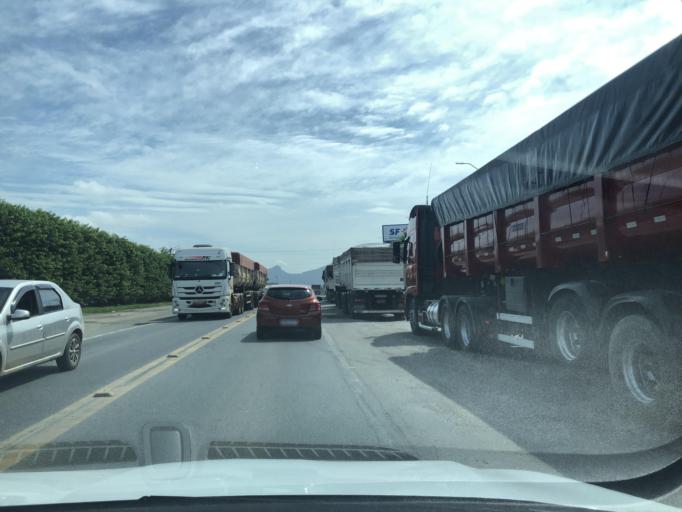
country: BR
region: Santa Catarina
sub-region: Sao Francisco Do Sul
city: Sao Francisco do Sul
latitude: -26.2593
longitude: -48.6247
